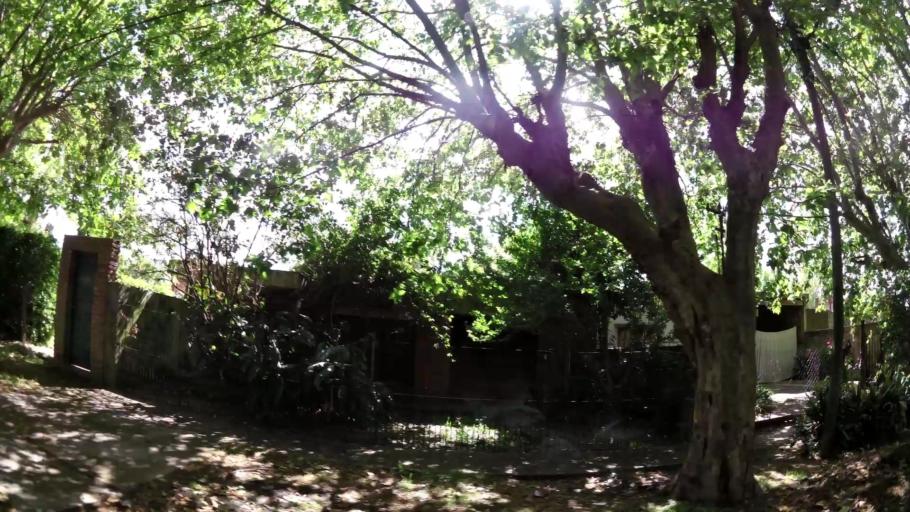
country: AR
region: Buenos Aires
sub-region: Partido de Quilmes
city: Quilmes
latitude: -34.8280
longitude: -58.1728
